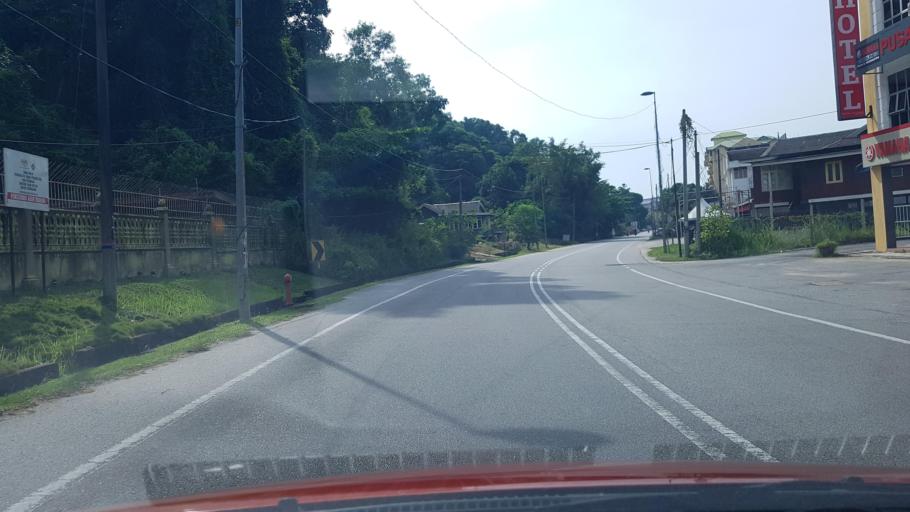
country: MY
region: Terengganu
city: Kuala Terengganu
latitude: 5.3201
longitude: 103.1401
